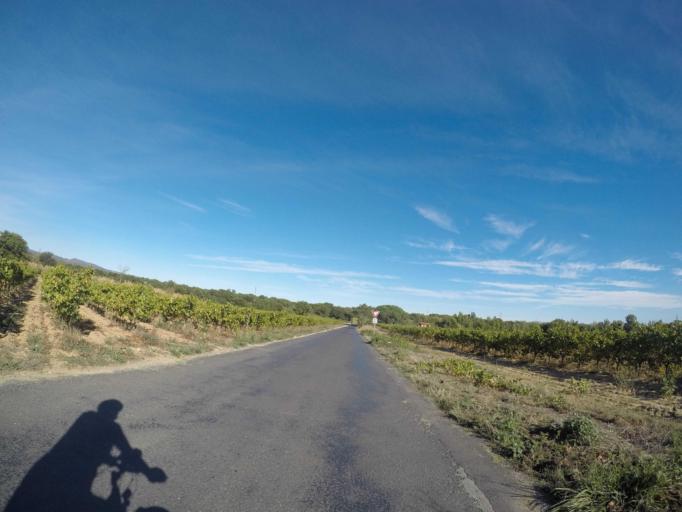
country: FR
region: Languedoc-Roussillon
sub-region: Departement des Pyrenees-Orientales
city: Trouillas
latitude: 42.5845
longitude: 2.8101
